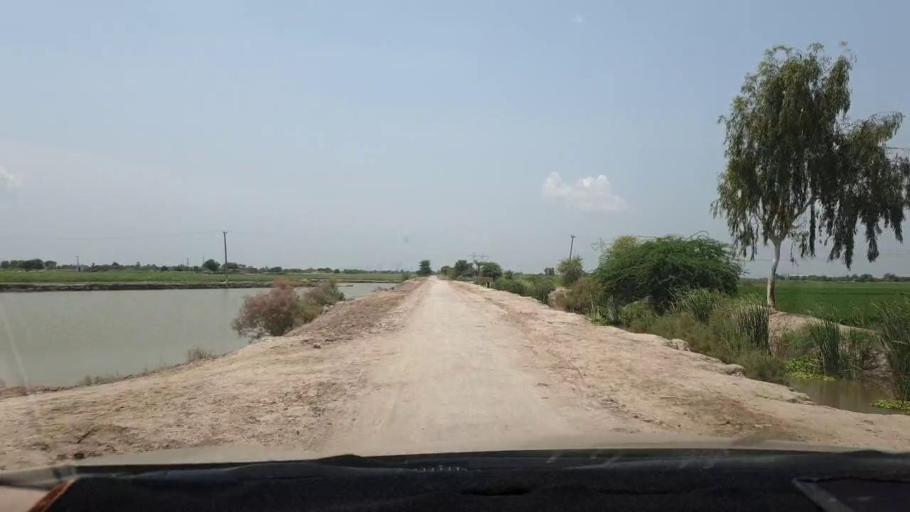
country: PK
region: Sindh
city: Naudero
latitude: 27.6685
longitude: 68.2871
